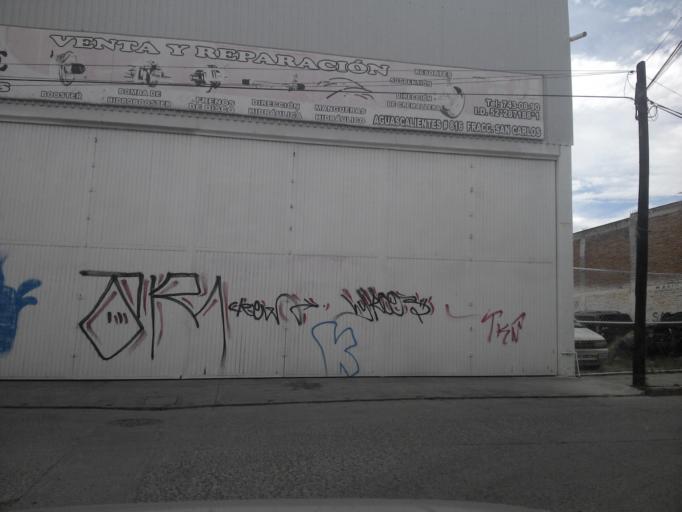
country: MX
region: Guanajuato
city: San Francisco del Rincon
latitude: 21.0094
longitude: -101.8561
